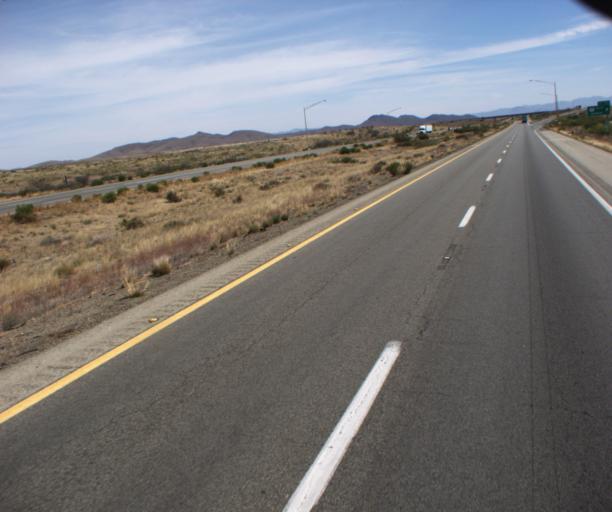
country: US
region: Arizona
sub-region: Cochise County
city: Willcox
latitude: 32.3578
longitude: -109.6891
